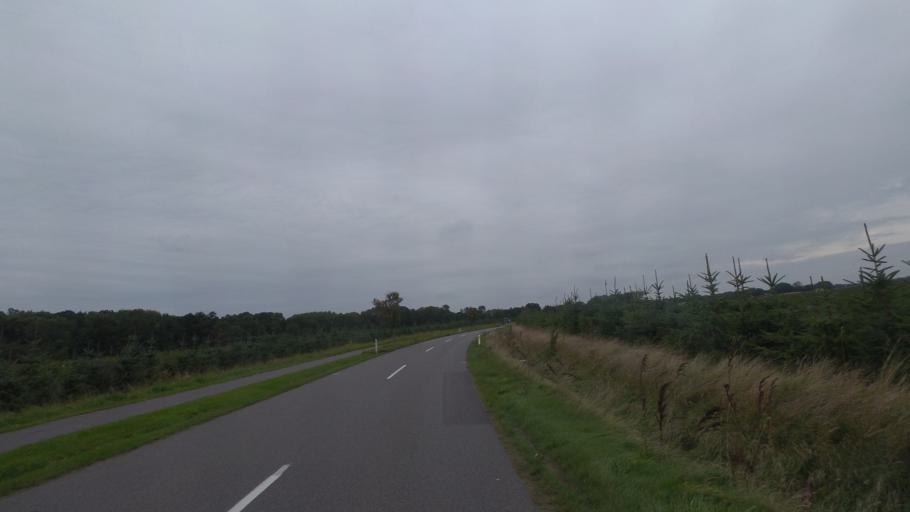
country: DK
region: Capital Region
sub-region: Bornholm Kommune
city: Akirkeby
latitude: 55.0025
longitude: 14.9999
